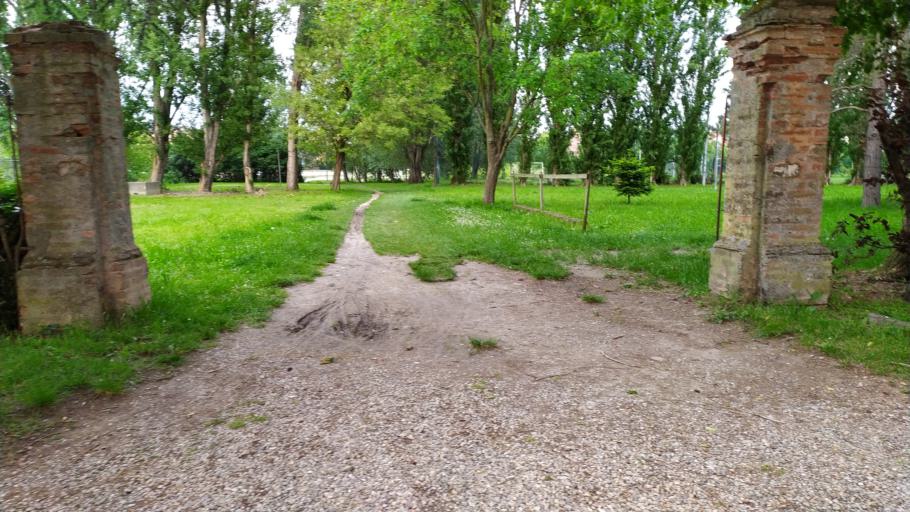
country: IT
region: Emilia-Romagna
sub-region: Provincia di Bologna
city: Castel Maggiore
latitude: 44.5826
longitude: 11.3584
